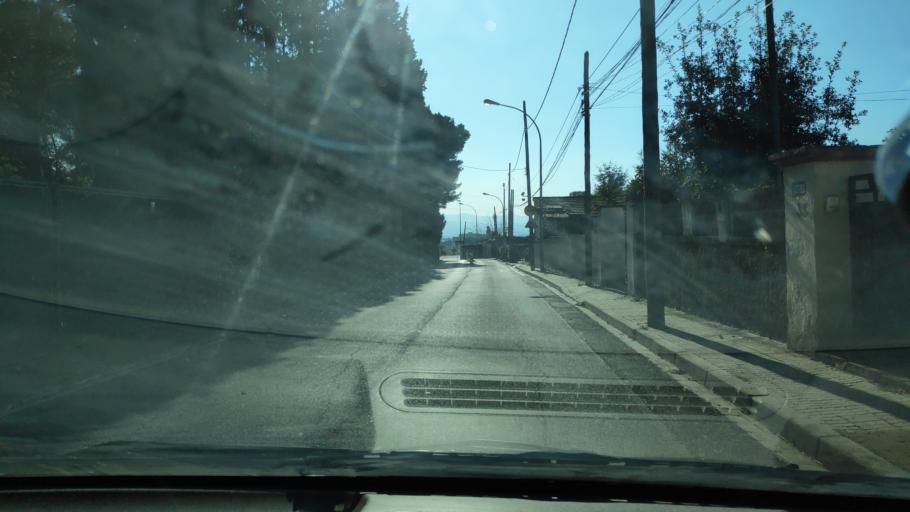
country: ES
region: Catalonia
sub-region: Provincia de Barcelona
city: Sant Cugat del Valles
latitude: 41.4938
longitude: 2.0813
